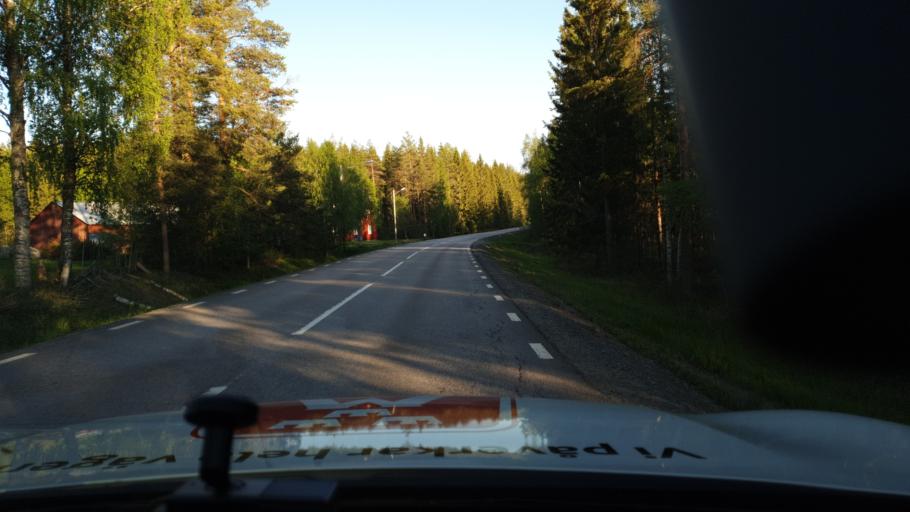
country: SE
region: Vaesterbotten
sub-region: Umea Kommun
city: Ersmark
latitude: 63.9612
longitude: 20.2912
